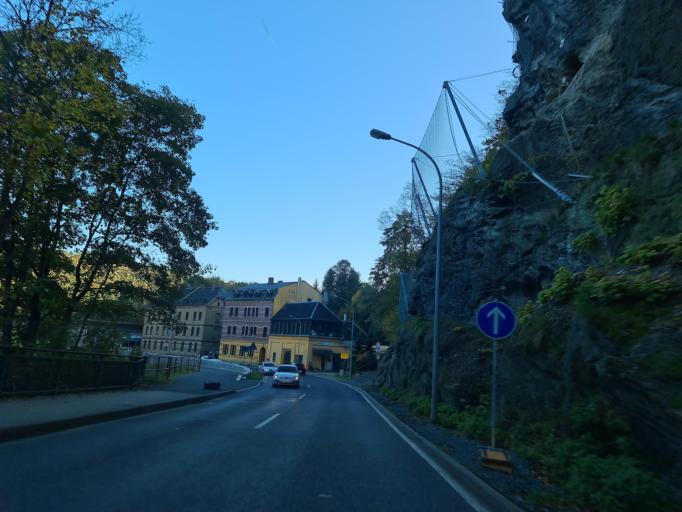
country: DE
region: Thuringia
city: Greiz
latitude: 50.6382
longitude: 12.1909
